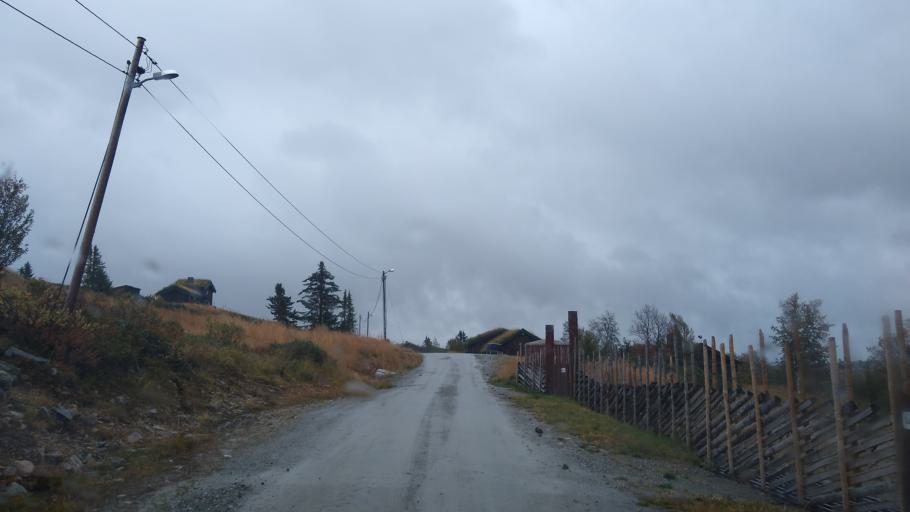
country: NO
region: Oppland
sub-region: Ringebu
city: Ringebu
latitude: 61.6725
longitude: 10.0956
